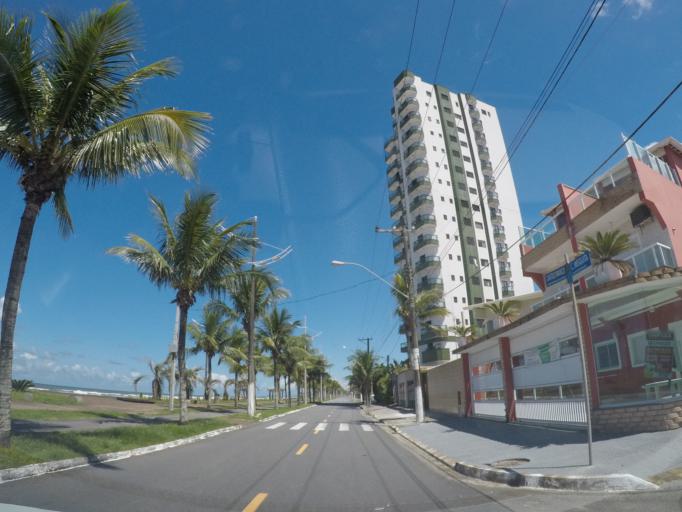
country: BR
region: Sao Paulo
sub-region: Mongagua
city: Mongagua
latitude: -24.0779
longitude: -46.5830
